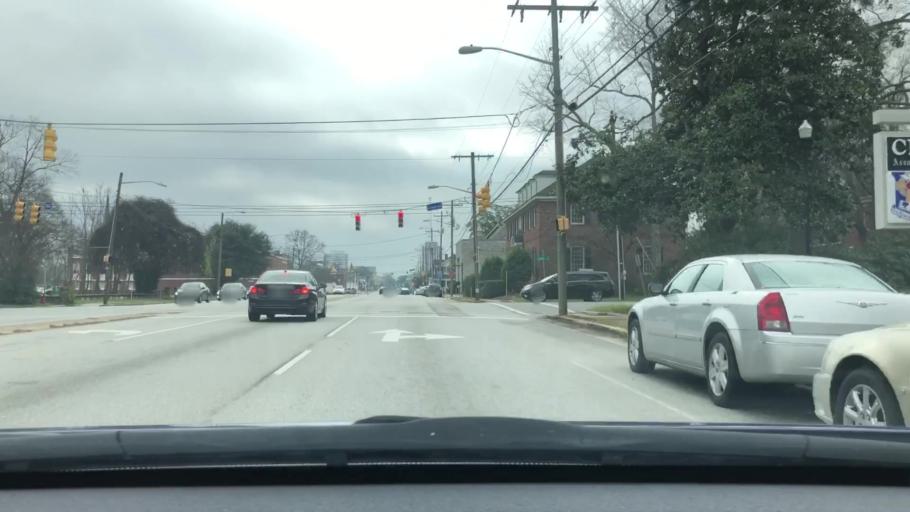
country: US
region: South Carolina
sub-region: Richland County
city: Columbia
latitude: 34.0111
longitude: -81.0325
